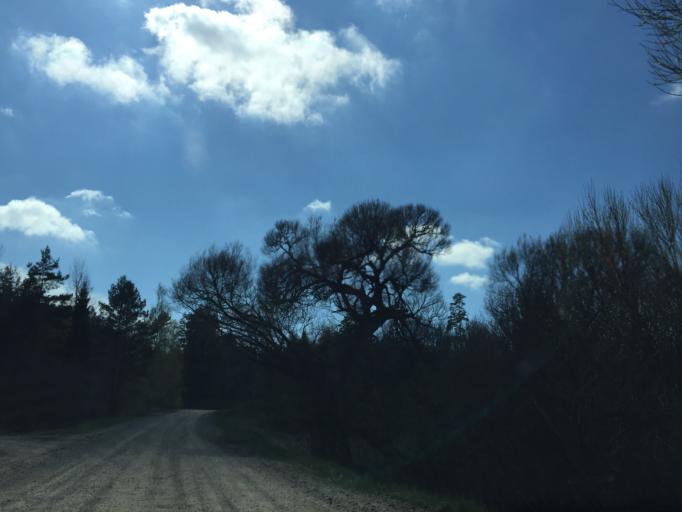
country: LV
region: Smiltene
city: Smiltene
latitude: 57.5816
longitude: 25.9398
